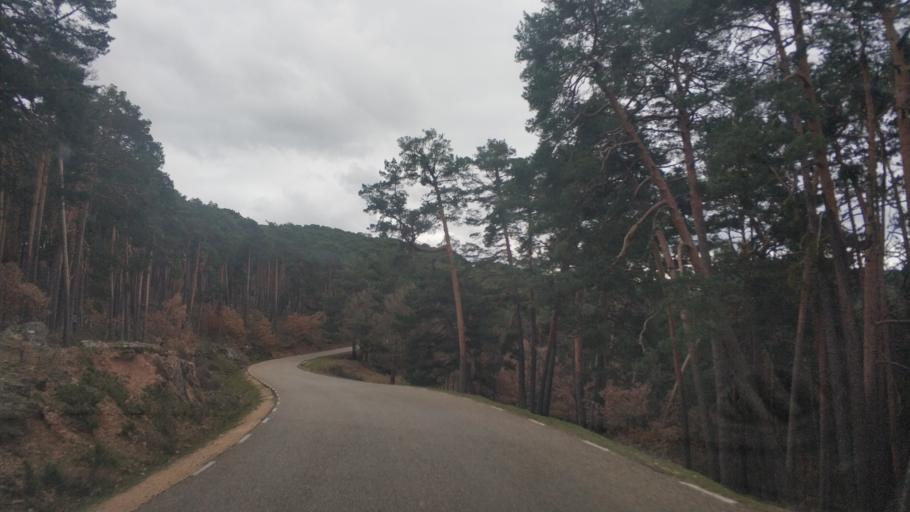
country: ES
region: Castille and Leon
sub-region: Provincia de Burgos
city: Canicosa de la Sierra
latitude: 41.9258
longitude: -3.0402
